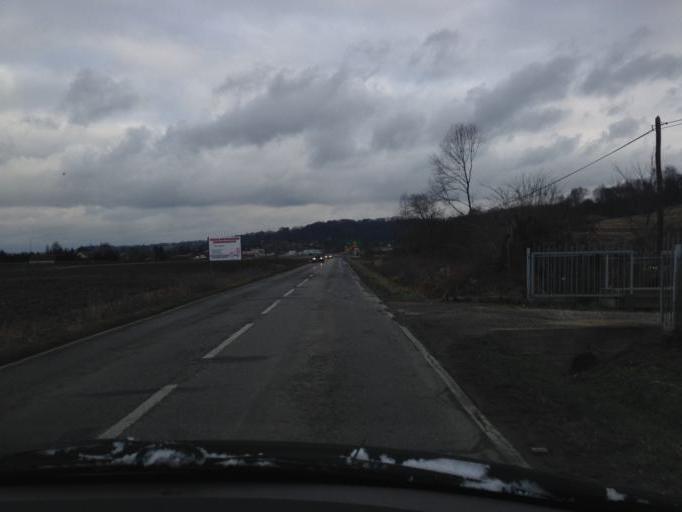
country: PL
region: Lesser Poland Voivodeship
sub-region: Powiat wielicki
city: Gdow
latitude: 49.8973
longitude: 20.2166
